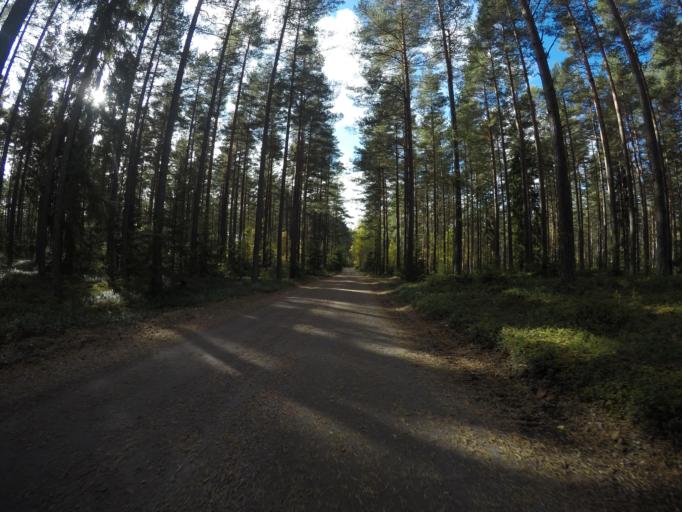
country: SE
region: Vaestmanland
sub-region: Kungsors Kommun
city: Kungsoer
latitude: 59.2978
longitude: 16.1123
